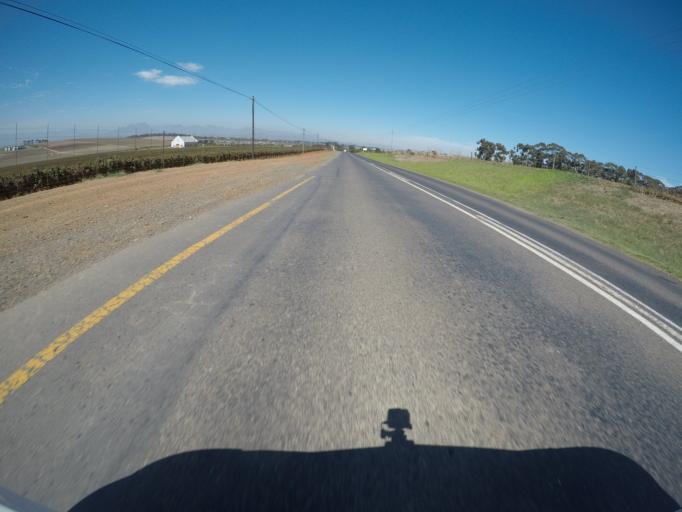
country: ZA
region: Western Cape
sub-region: City of Cape Town
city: Kraaifontein
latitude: -33.8040
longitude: 18.6205
